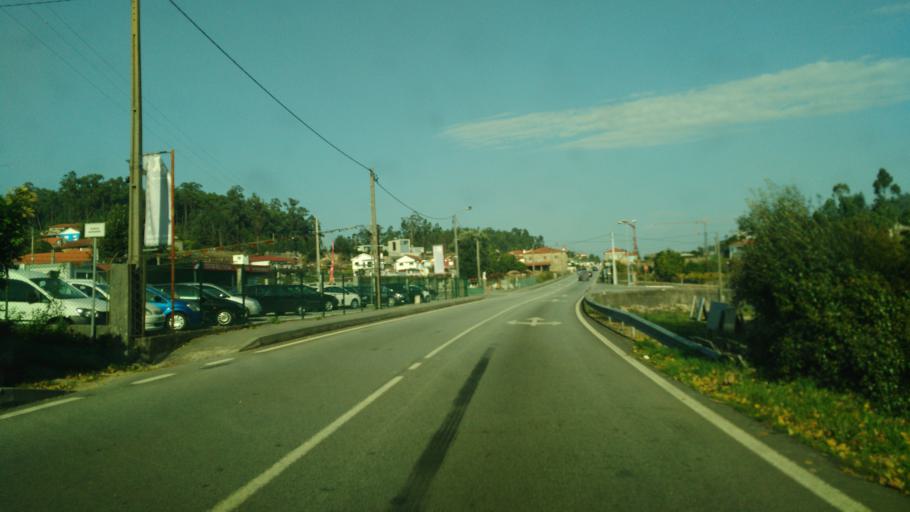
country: PT
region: Braga
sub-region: Braga
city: Oliveira
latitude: 41.4838
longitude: -8.4787
